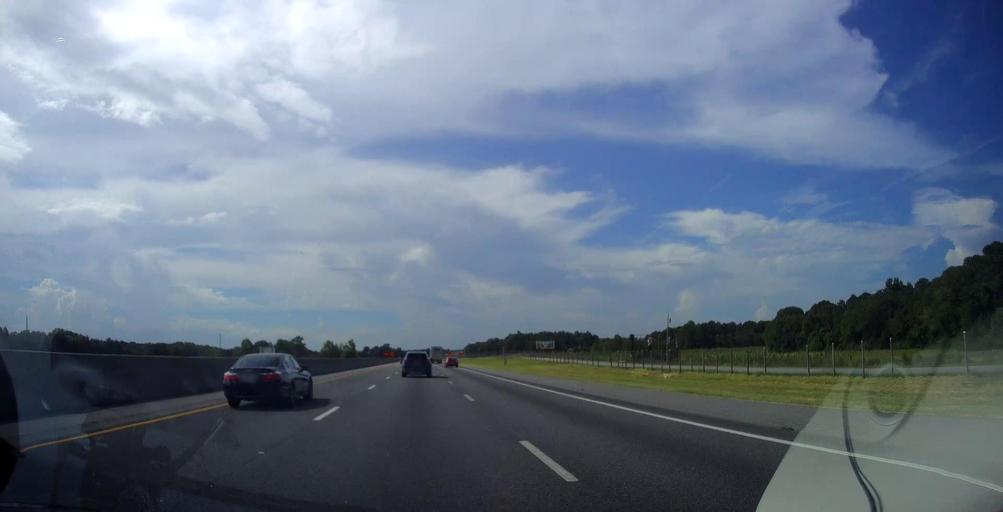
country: US
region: Georgia
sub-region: Tift County
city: Tifton
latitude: 31.5875
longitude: -83.5550
